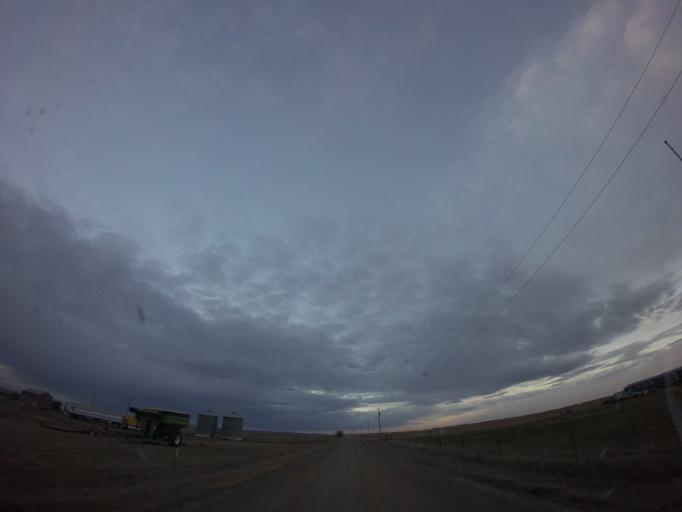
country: US
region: Montana
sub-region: Yellowstone County
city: Laurel
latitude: 45.9436
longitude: -108.7356
